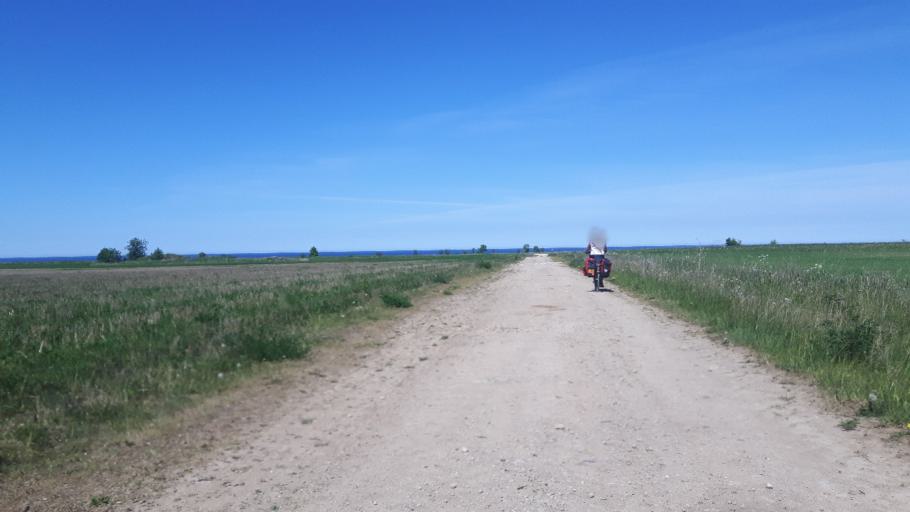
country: EE
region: Ida-Virumaa
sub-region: Toila vald
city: Voka
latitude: 59.4120
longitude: 27.6470
